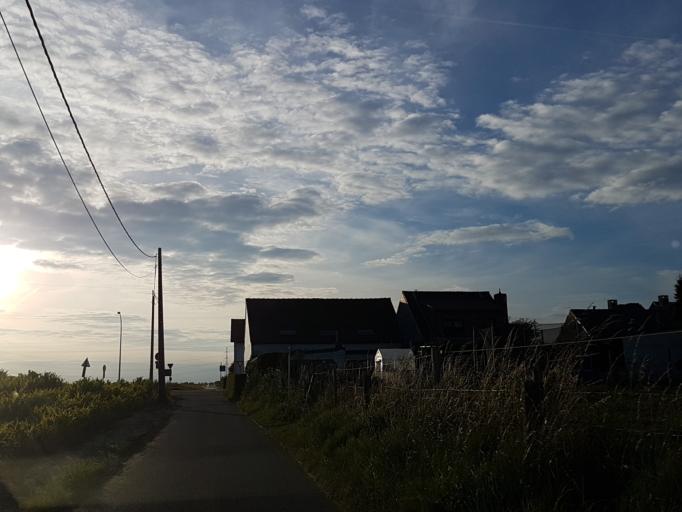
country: BE
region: Flanders
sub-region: Provincie Vlaams-Brabant
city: Merchtem
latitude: 50.9805
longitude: 4.2537
